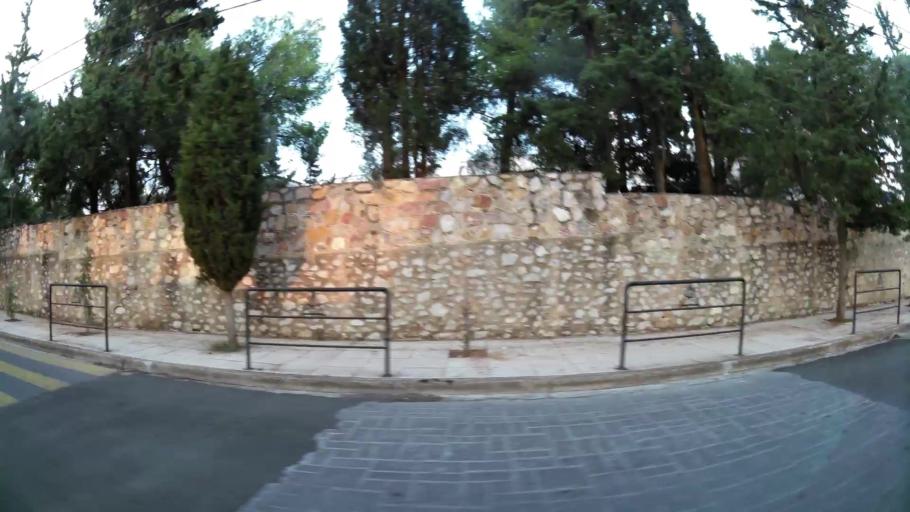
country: GR
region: Attica
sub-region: Nomarchia Athinas
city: Psychiko
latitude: 38.0160
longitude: 23.7788
